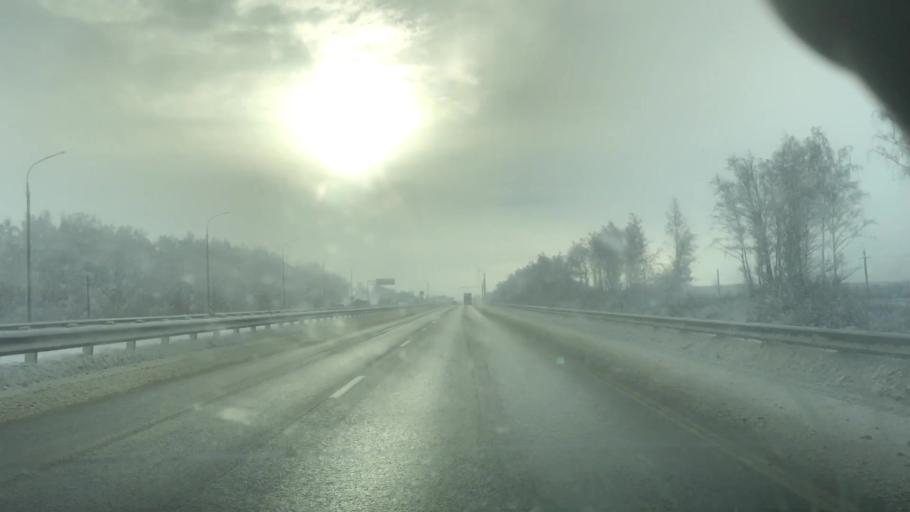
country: RU
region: Tula
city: Venev
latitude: 54.3489
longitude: 38.1549
